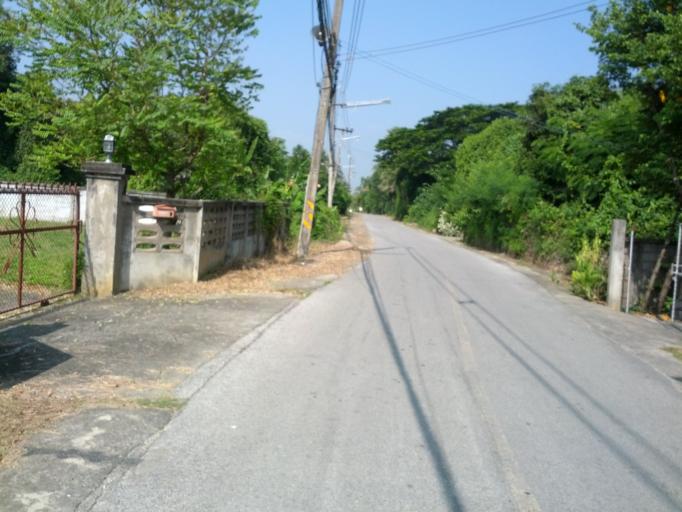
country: TH
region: Chiang Mai
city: San Kamphaeng
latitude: 18.8024
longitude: 99.0984
